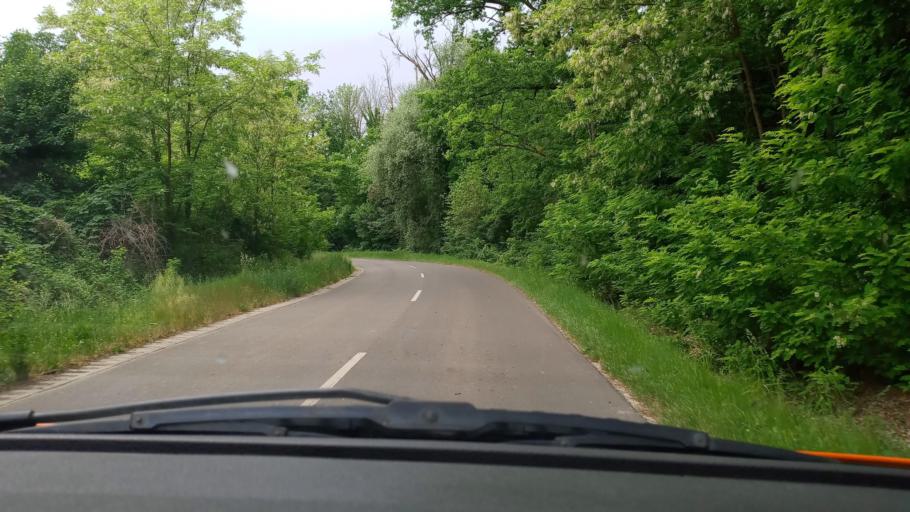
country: HU
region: Baranya
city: Vajszlo
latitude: 45.8419
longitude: 17.9759
